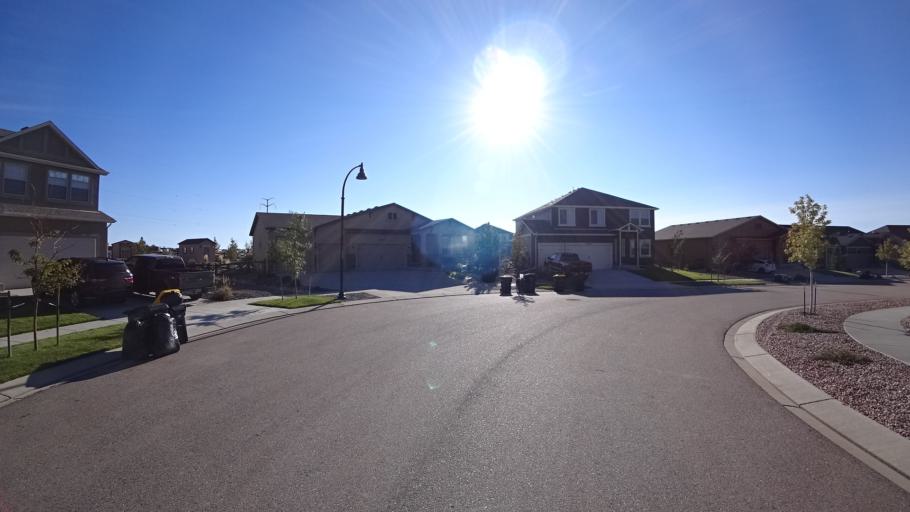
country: US
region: Colorado
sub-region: El Paso County
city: Black Forest
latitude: 38.9368
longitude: -104.6677
